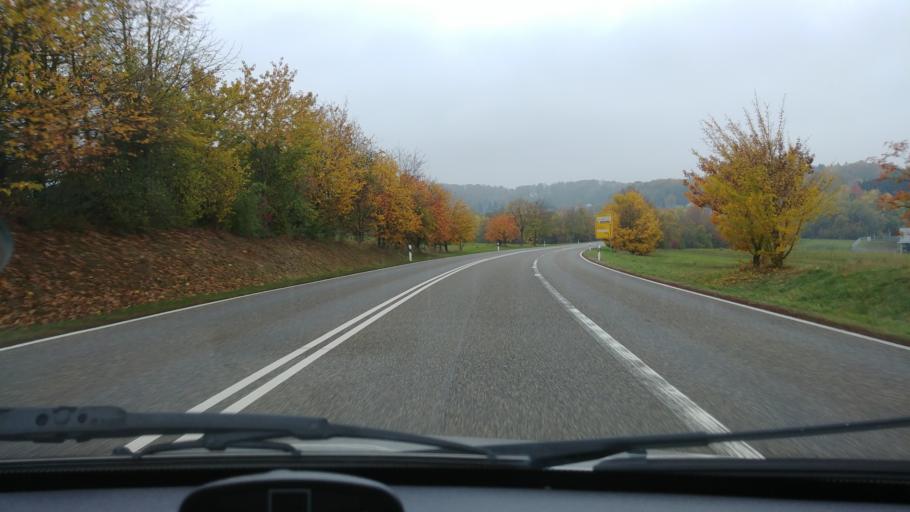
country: DE
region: Rheinland-Pfalz
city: Willmenrod
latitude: 50.5531
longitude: 7.9662
